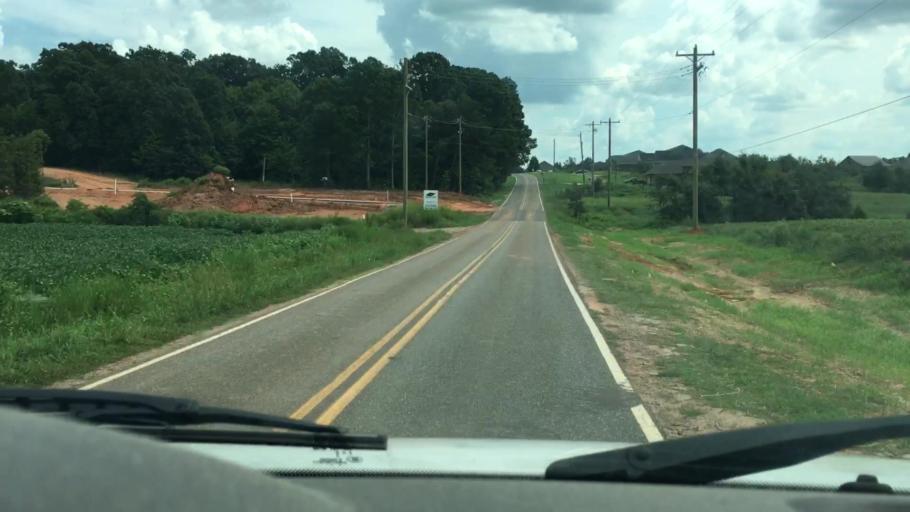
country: US
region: North Carolina
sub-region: Iredell County
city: Troutman
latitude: 35.6666
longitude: -80.8301
